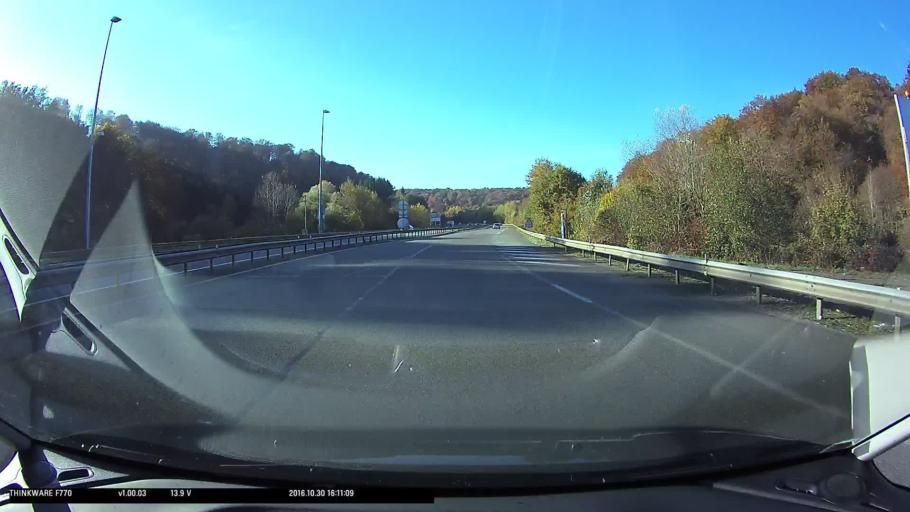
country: FR
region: Franche-Comte
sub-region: Departement du Doubs
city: Colombier-Fontaine
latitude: 47.4264
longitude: 6.6690
